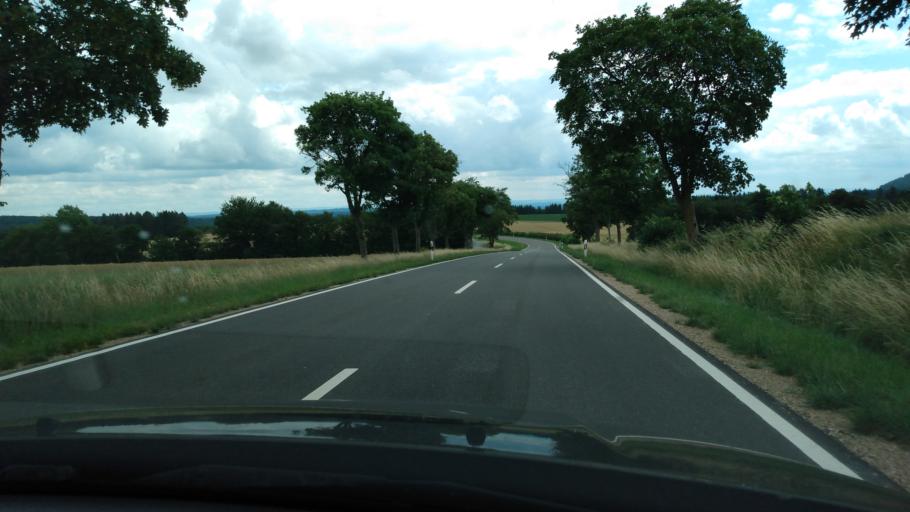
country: DE
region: Rheinland-Pfalz
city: Bleckhausen
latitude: 50.1131
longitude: 6.7862
